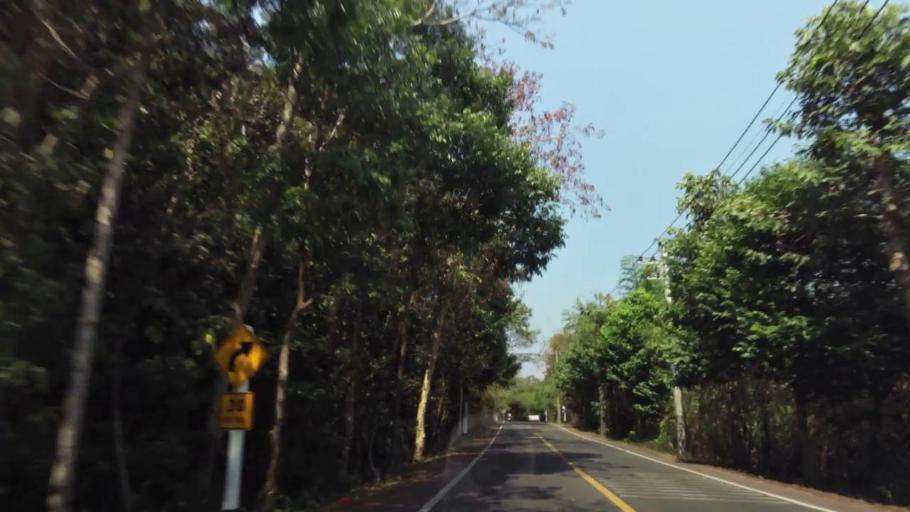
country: TH
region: Chanthaburi
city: Tha Mai
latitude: 12.5373
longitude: 101.9469
